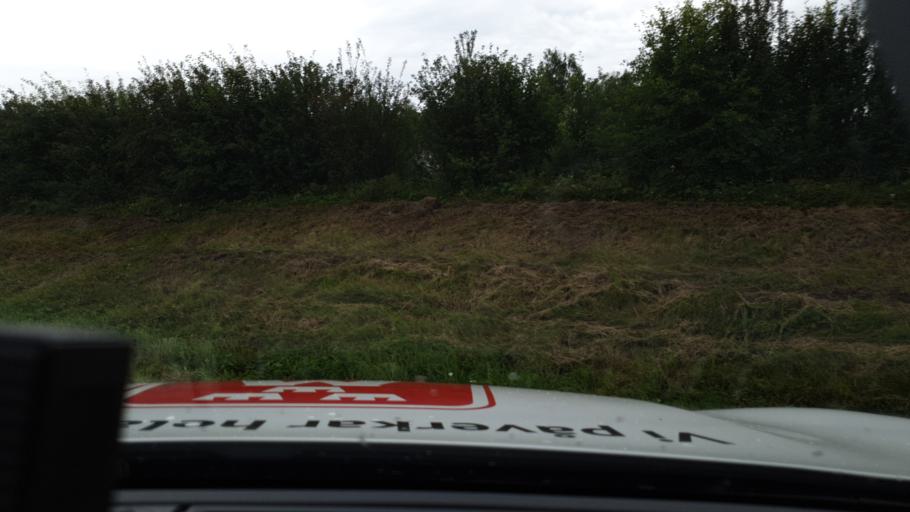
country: SE
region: Norrbotten
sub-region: Bodens Kommun
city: Saevast
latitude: 65.8724
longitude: 21.8859
